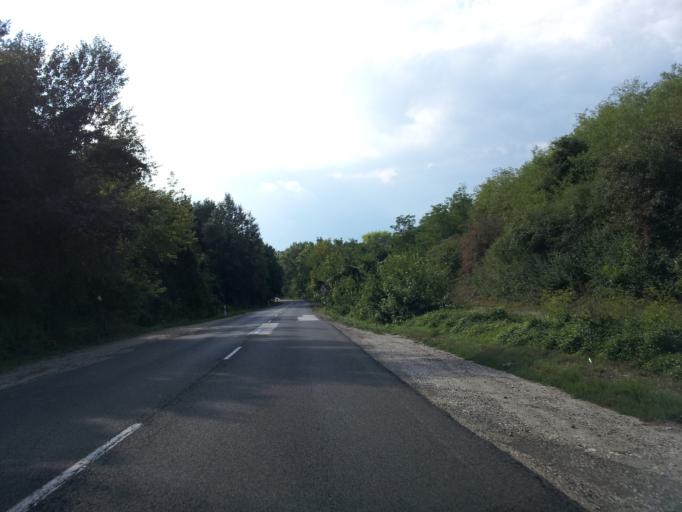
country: HU
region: Pest
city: Dunabogdany
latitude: 47.8131
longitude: 19.0819
